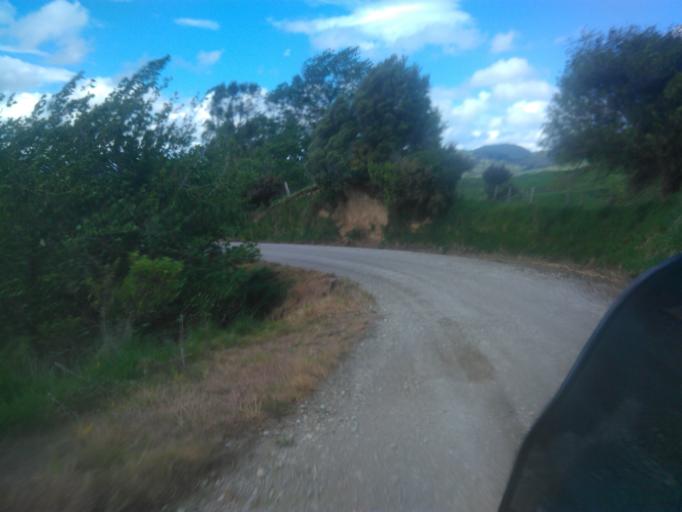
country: NZ
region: Hawke's Bay
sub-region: Wairoa District
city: Wairoa
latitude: -38.7699
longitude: 177.6394
